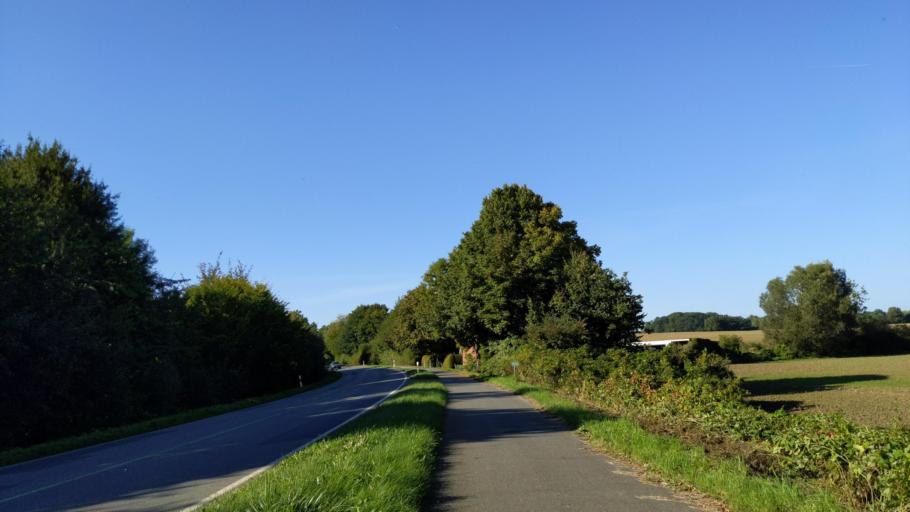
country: DE
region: Schleswig-Holstein
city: Ahrensbok
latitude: 53.9684
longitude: 10.6004
